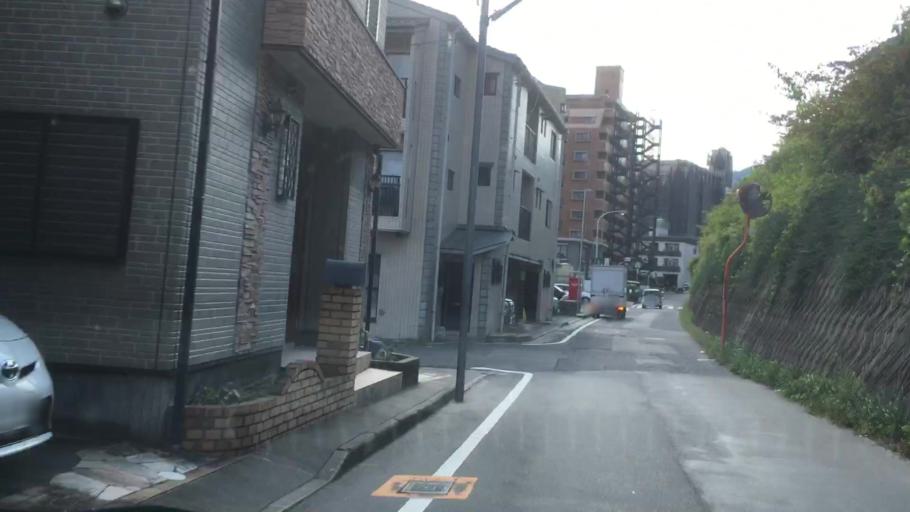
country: JP
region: Hiroshima
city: Hiroshima-shi
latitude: 34.3890
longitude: 132.4062
